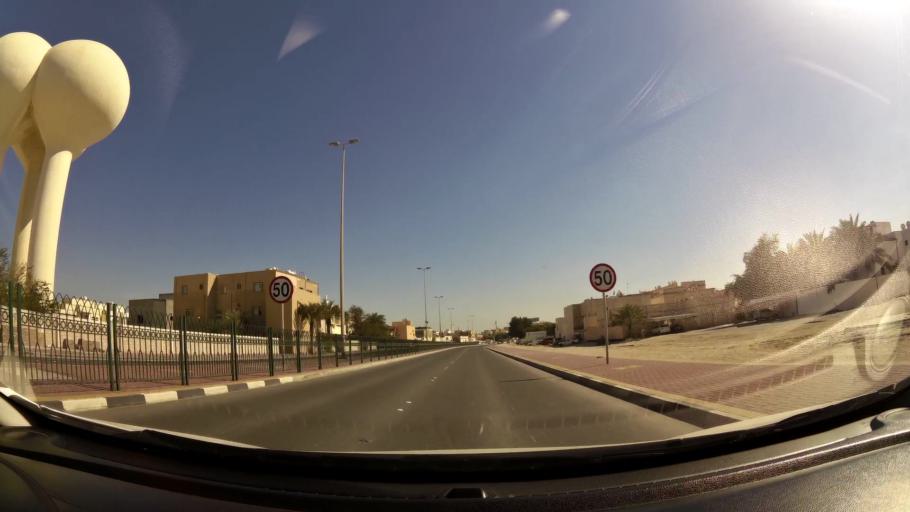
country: BH
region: Muharraq
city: Al Hadd
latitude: 26.2491
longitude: 50.6517
